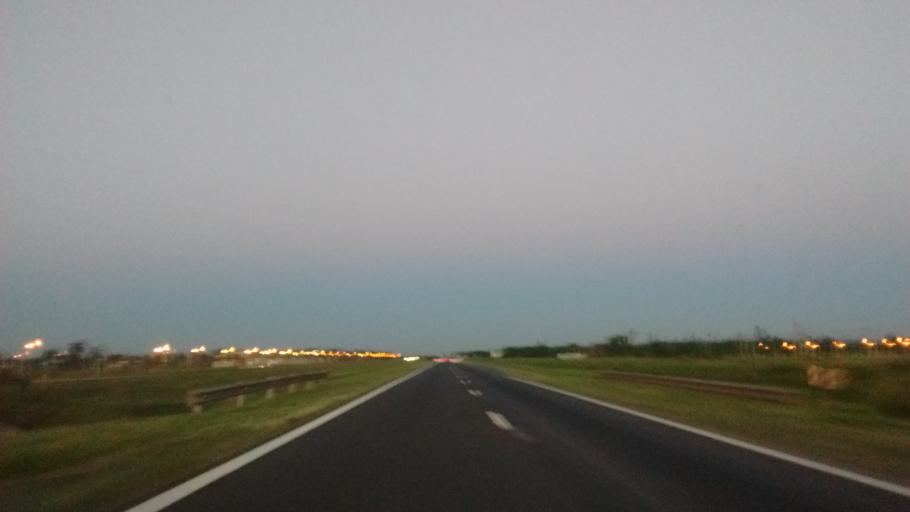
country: AR
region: Santa Fe
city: Roldan
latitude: -32.9305
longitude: -60.8718
